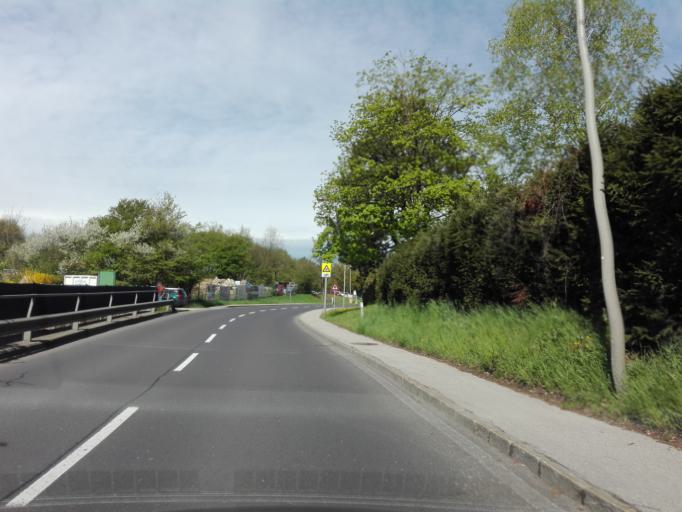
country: AT
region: Upper Austria
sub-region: Linz Stadt
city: Linz
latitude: 48.3097
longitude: 14.2658
